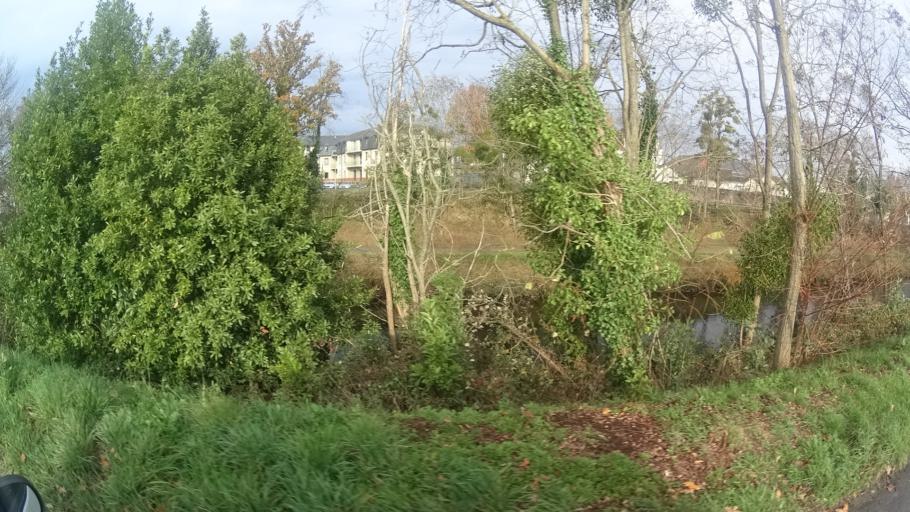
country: FR
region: Brittany
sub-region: Departement d'Ille-et-Vilaine
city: Redon
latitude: 47.6499
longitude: -2.0909
